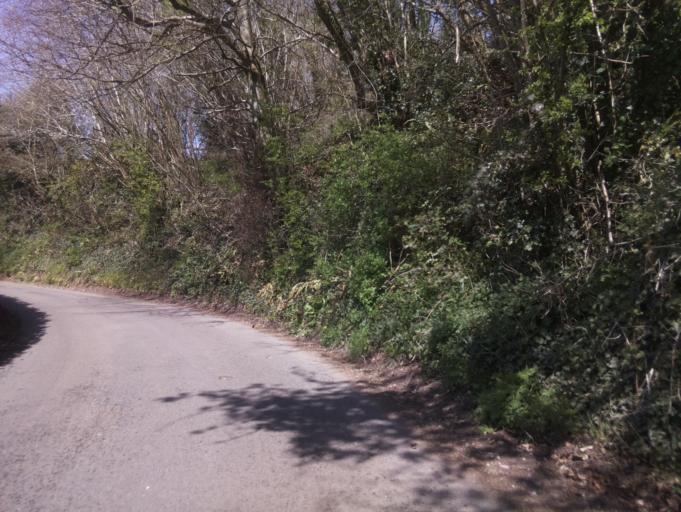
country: GB
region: Wales
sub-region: Monmouthshire
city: Caldicot
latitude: 51.6467
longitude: -2.7403
